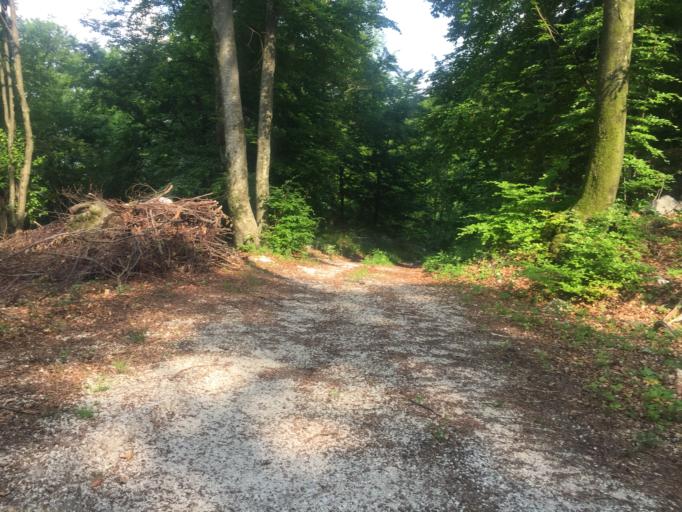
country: IT
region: Friuli Venezia Giulia
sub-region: Provincia di Udine
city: Cavazzo Carnico
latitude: 46.3495
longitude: 13.0240
